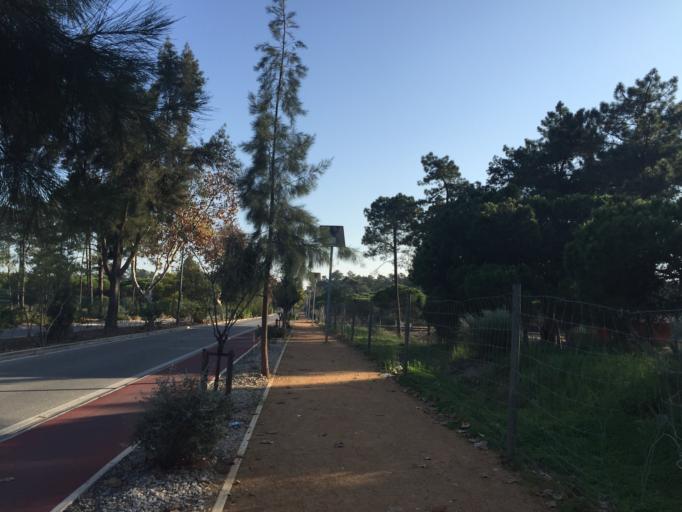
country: PT
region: Faro
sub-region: Vila Real de Santo Antonio
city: Vila Real de Santo Antonio
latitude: 37.1901
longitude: -7.4238
